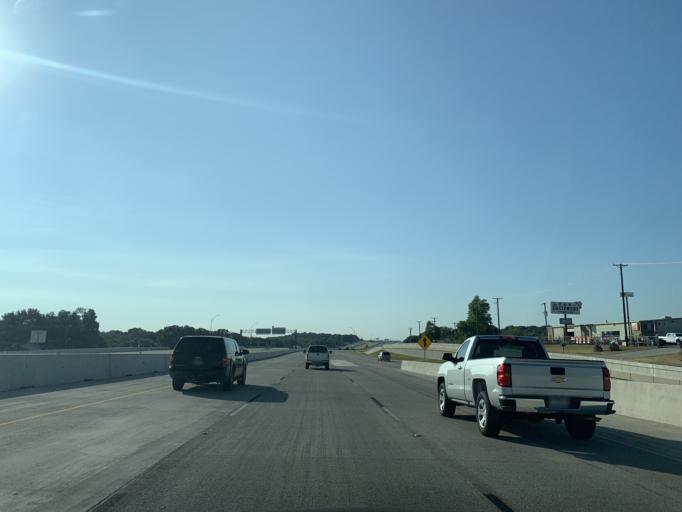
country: US
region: Texas
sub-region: Tarrant County
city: Lakeside
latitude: 32.8534
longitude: -97.5093
